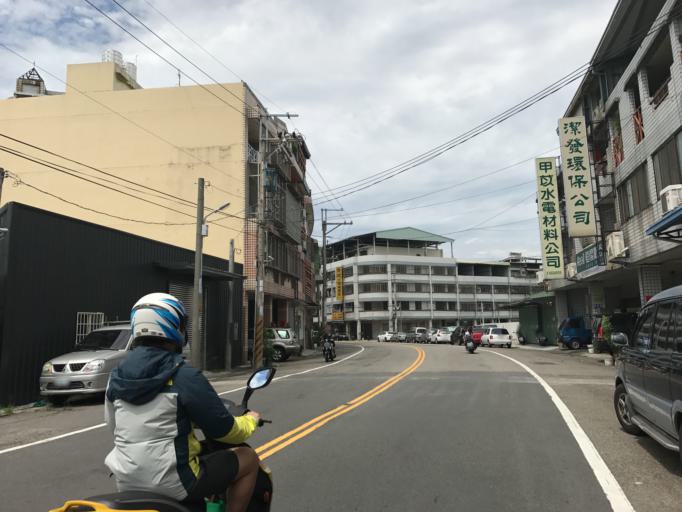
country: TW
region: Taiwan
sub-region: Taichung City
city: Taichung
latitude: 24.0829
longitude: 120.7005
